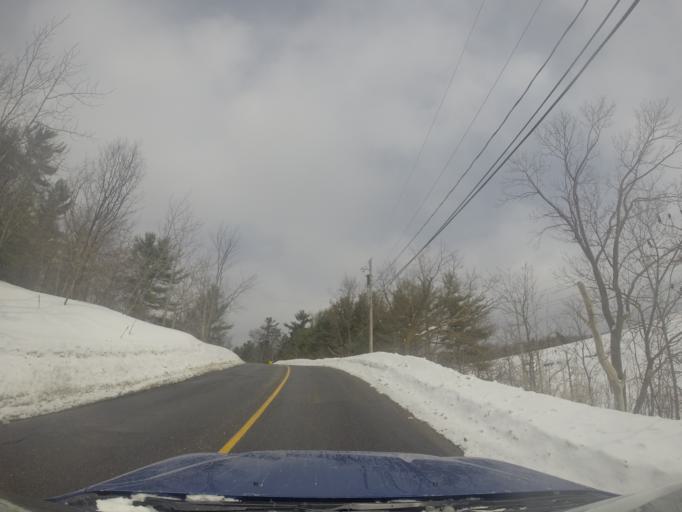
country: CA
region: Ontario
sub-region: Parry Sound District
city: Parry Sound
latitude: 45.3672
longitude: -80.0253
